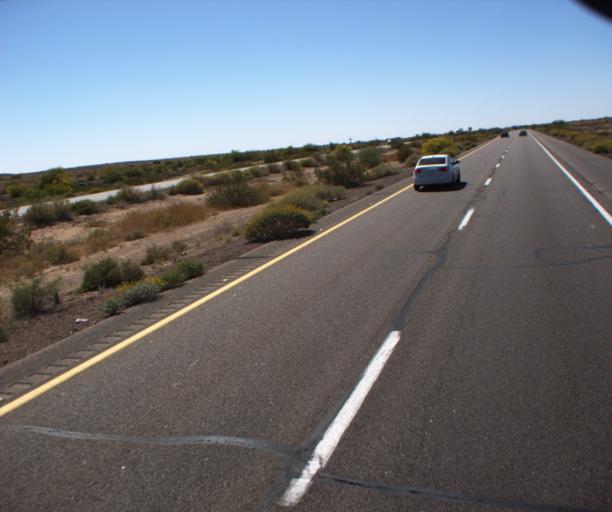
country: US
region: Arizona
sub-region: Maricopa County
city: Gila Bend
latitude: 32.8785
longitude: -113.1124
